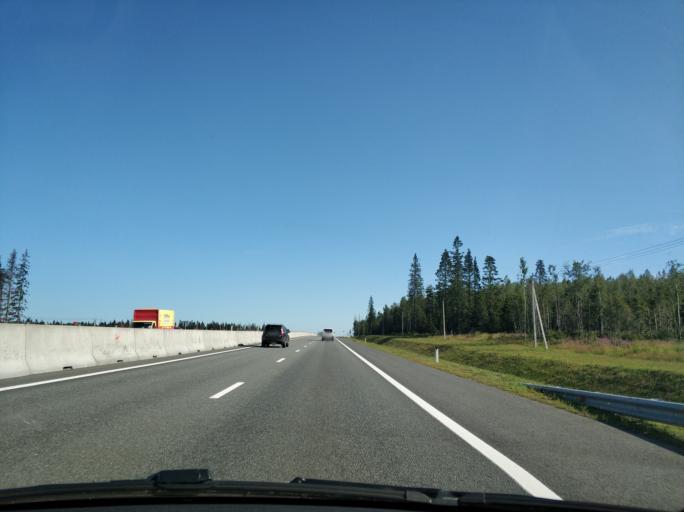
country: RU
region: Leningrad
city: Sosnovo
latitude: 60.4867
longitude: 30.1958
